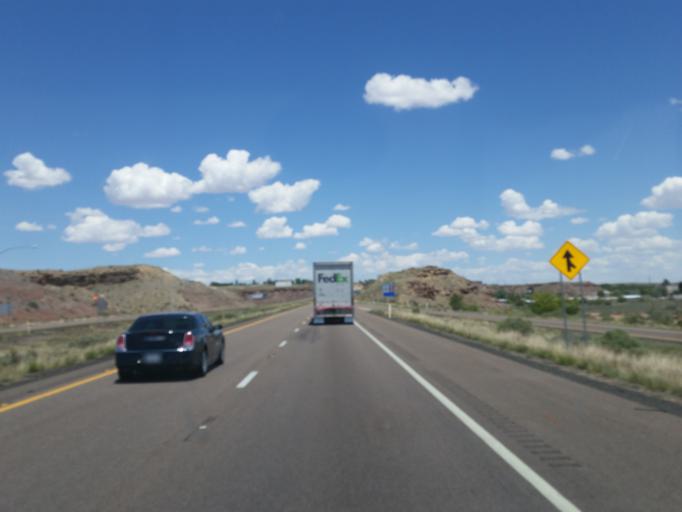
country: US
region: Arizona
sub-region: Navajo County
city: Holbrook
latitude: 34.9067
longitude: -110.1831
